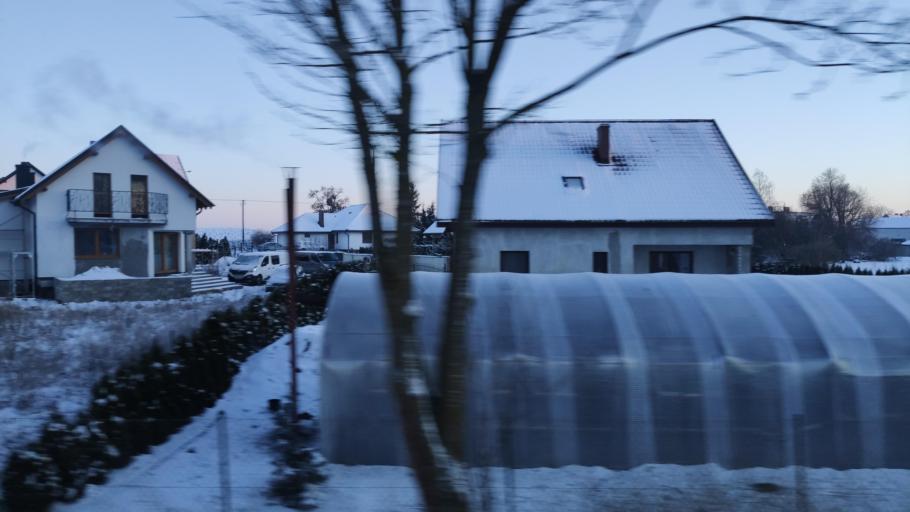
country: PL
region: Kujawsko-Pomorskie
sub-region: Powiat zninski
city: Znin
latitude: 52.8671
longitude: 17.7934
